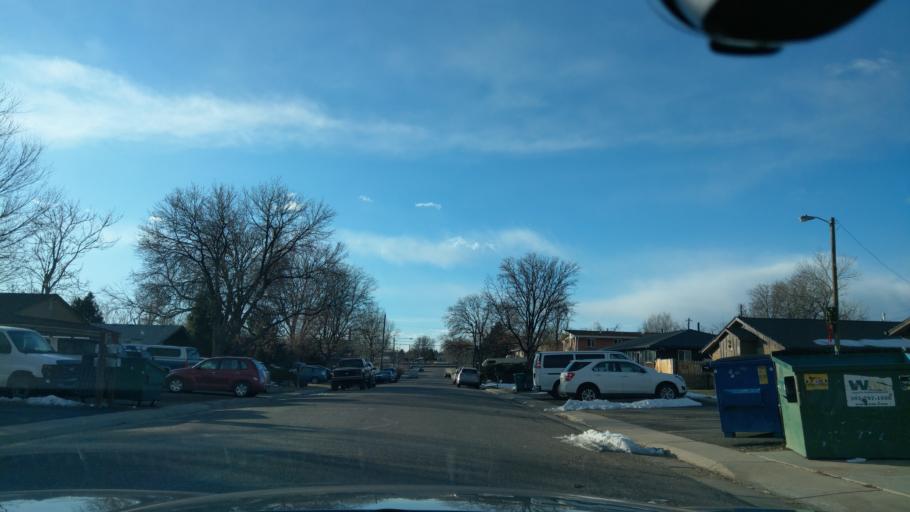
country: US
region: Colorado
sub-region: Jefferson County
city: Lakewood
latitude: 39.7286
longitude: -105.1149
